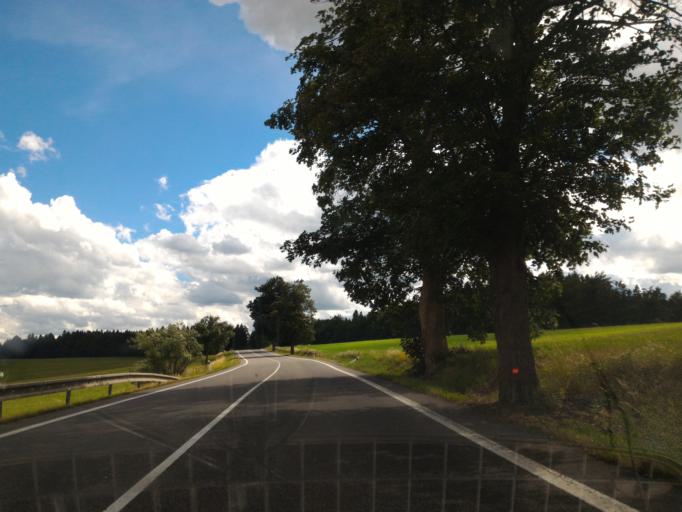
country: CZ
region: Vysocina
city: Bohdalov
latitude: 49.4704
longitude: 15.8255
